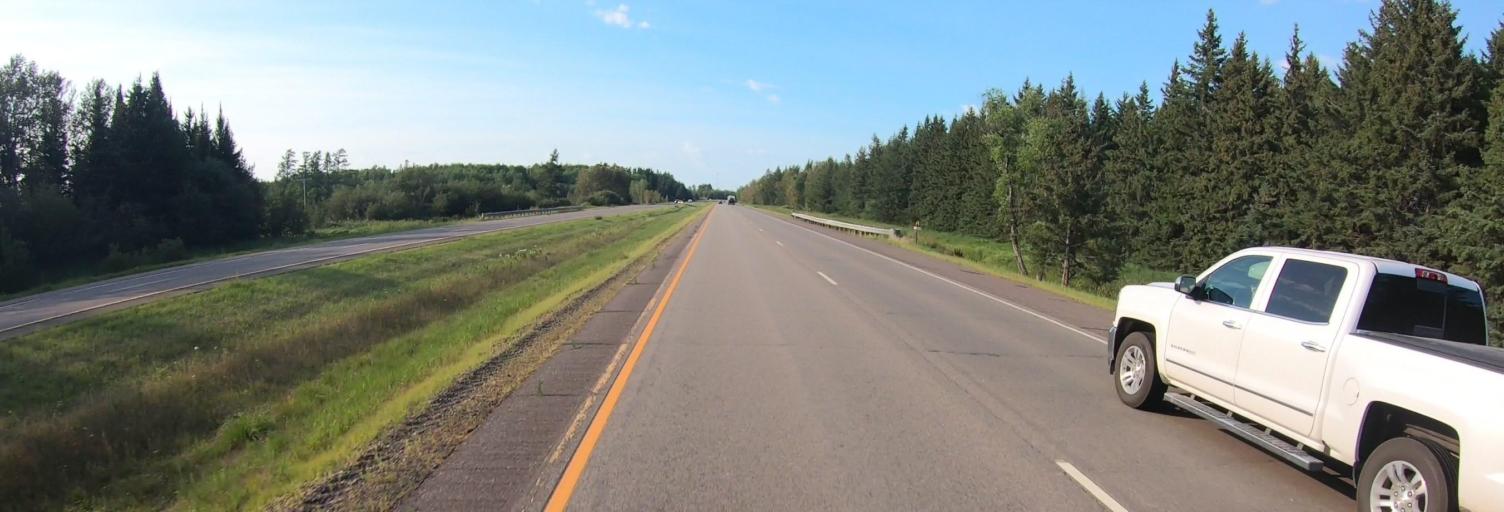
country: US
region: Minnesota
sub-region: Saint Louis County
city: Eveleth
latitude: 47.1322
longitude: -92.4721
